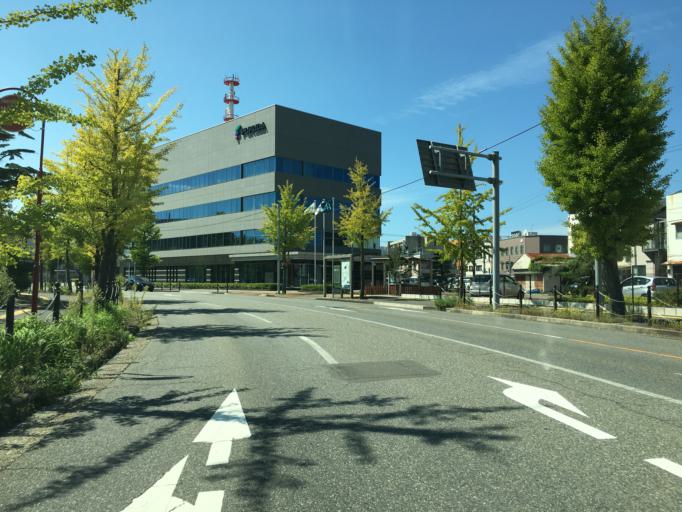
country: JP
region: Niigata
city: Niigata-shi
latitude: 37.9139
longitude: 139.0361
